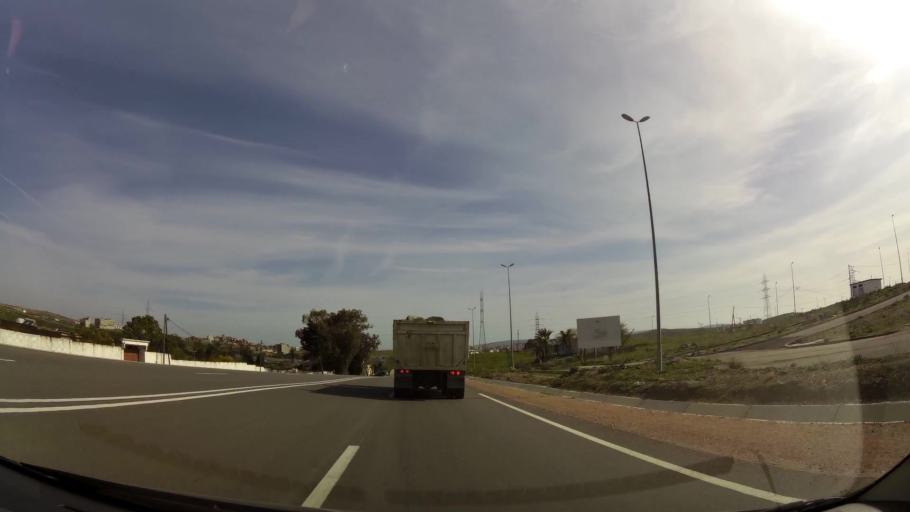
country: MA
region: Tanger-Tetouan
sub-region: Tanger-Assilah
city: Tangier
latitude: 35.7041
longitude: -5.8160
